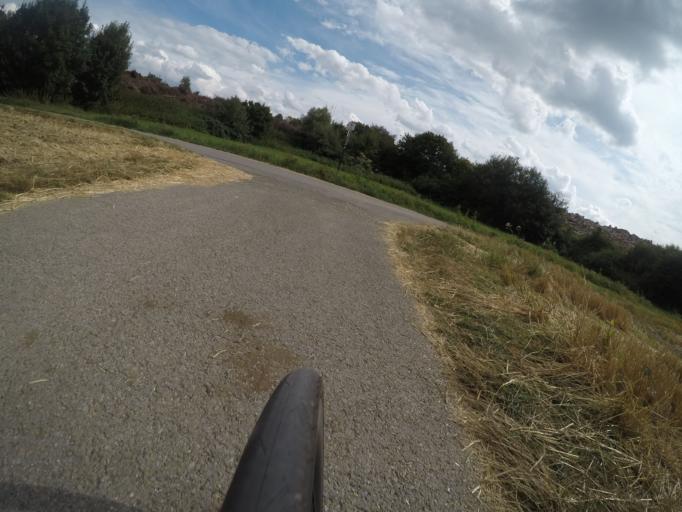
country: DE
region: Baden-Wuerttemberg
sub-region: Regierungsbezirk Stuttgart
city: Weil der Stadt
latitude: 48.7615
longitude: 8.8765
